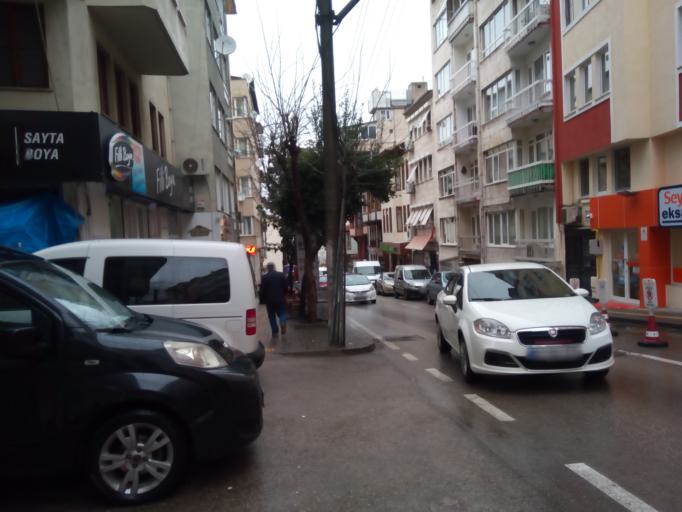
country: TR
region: Bursa
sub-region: Osmangazi
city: Bursa
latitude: 40.1810
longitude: 29.0616
